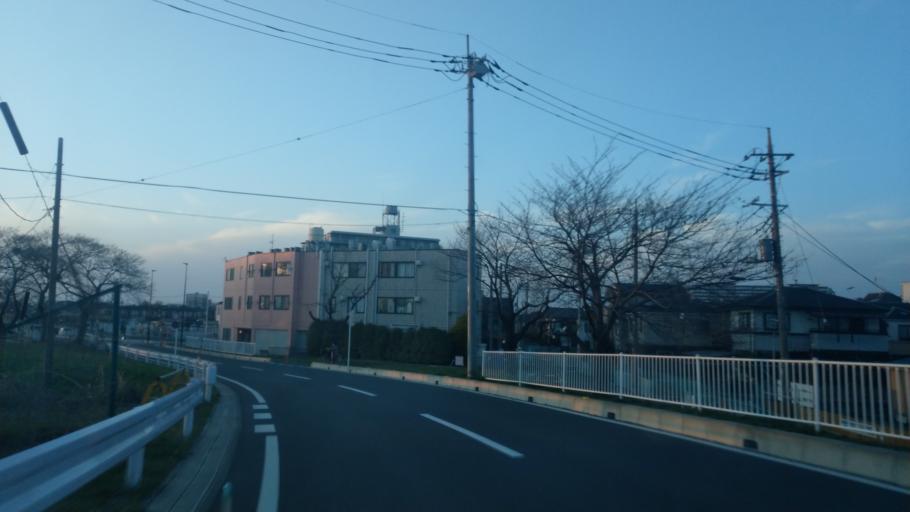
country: JP
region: Saitama
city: Yono
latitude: 35.8527
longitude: 139.6158
